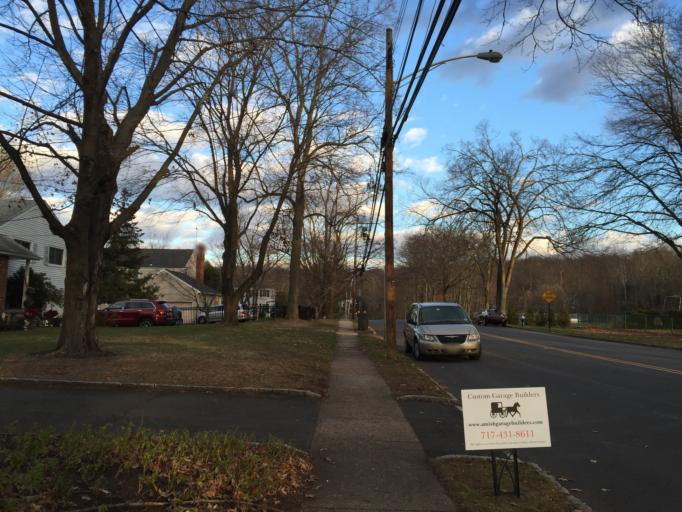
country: US
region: New Jersey
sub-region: Union County
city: New Providence
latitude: 40.6997
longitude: -74.3927
